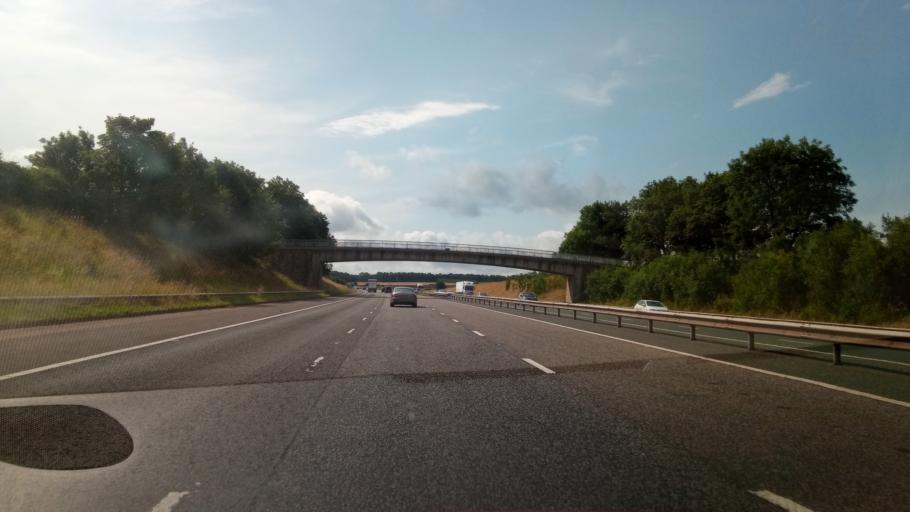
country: GB
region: England
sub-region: Cumbria
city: Penrith
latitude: 54.6239
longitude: -2.7219
